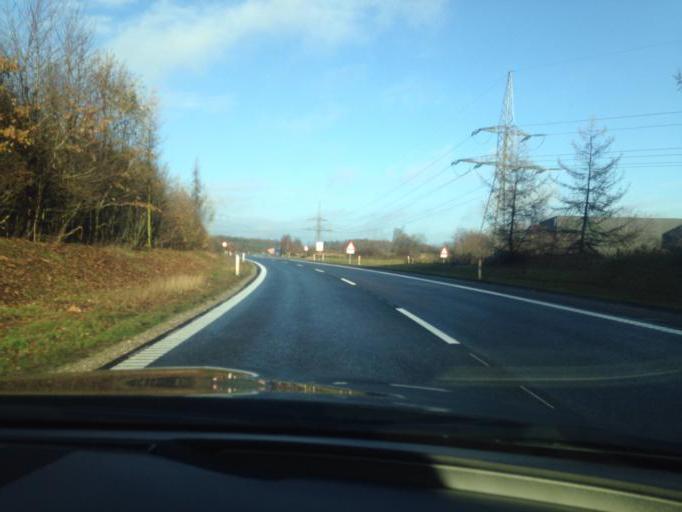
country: DK
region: South Denmark
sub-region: Kolding Kommune
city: Kolding
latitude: 55.5147
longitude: 9.4386
